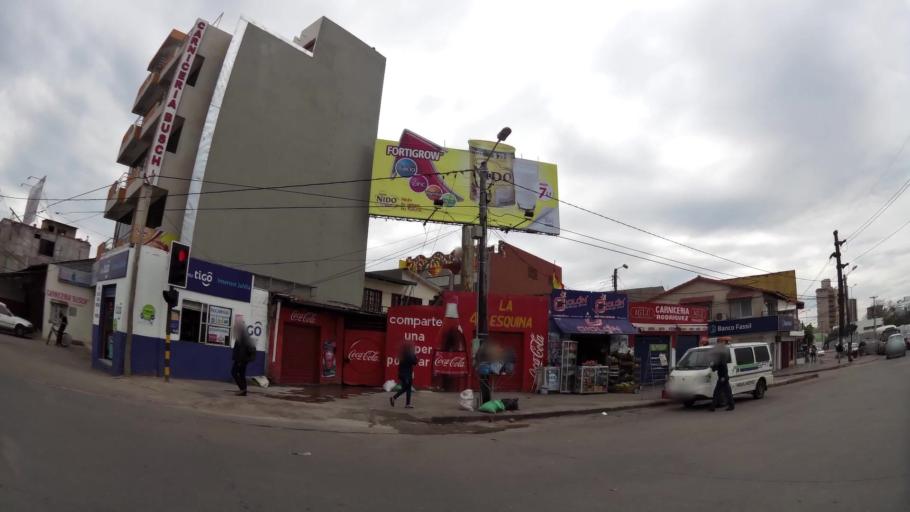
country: BO
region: Santa Cruz
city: Santa Cruz de la Sierra
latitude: -17.7721
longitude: -63.2029
